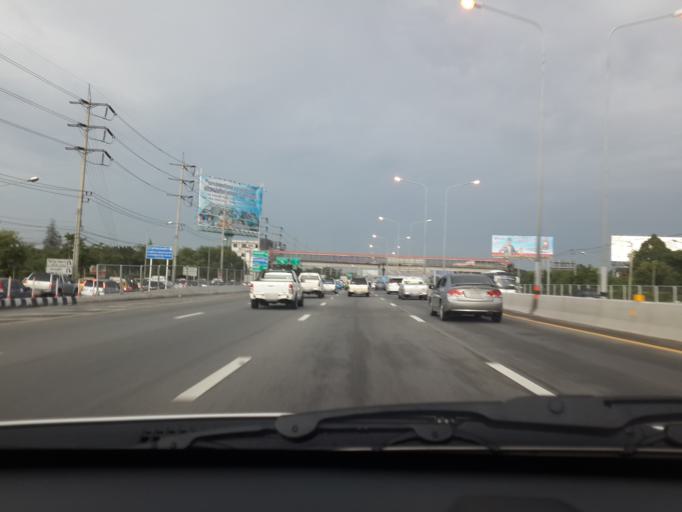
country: TH
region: Bangkok
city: Suan Luang
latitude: 13.7394
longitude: 100.6515
